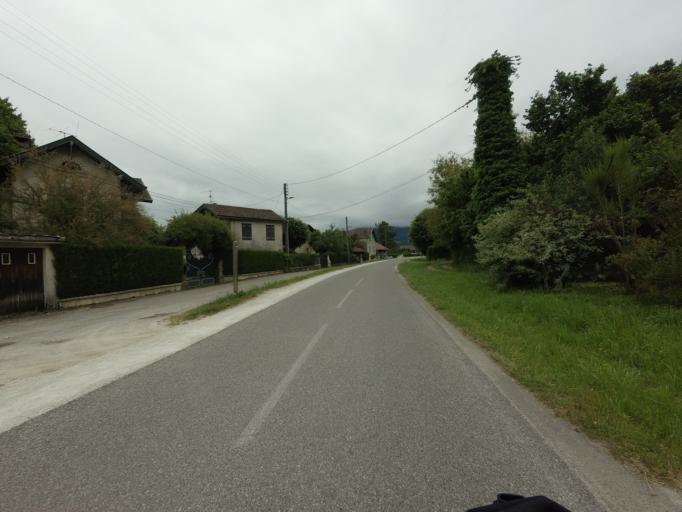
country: FR
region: Rhone-Alpes
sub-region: Departement de la Haute-Savoie
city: Sevrier
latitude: 45.8667
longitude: 6.1435
